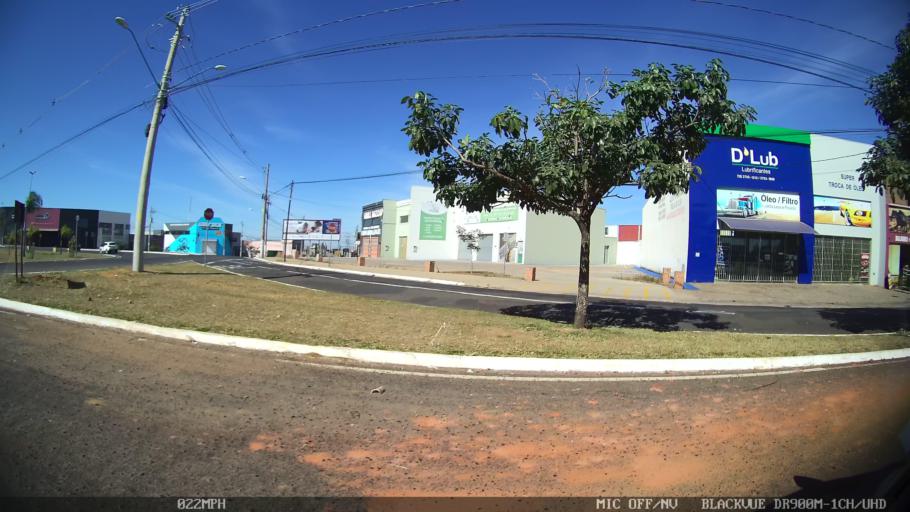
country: BR
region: Sao Paulo
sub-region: Franca
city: Franca
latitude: -20.5401
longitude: -47.3613
